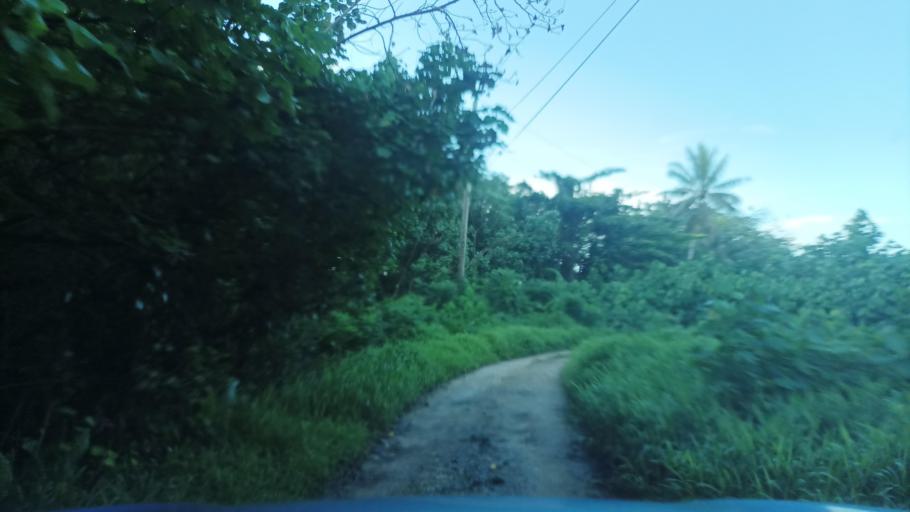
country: FM
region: Pohnpei
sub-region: Kolonia Municipality
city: Kolonia Town
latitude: 6.9781
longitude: 158.1806
